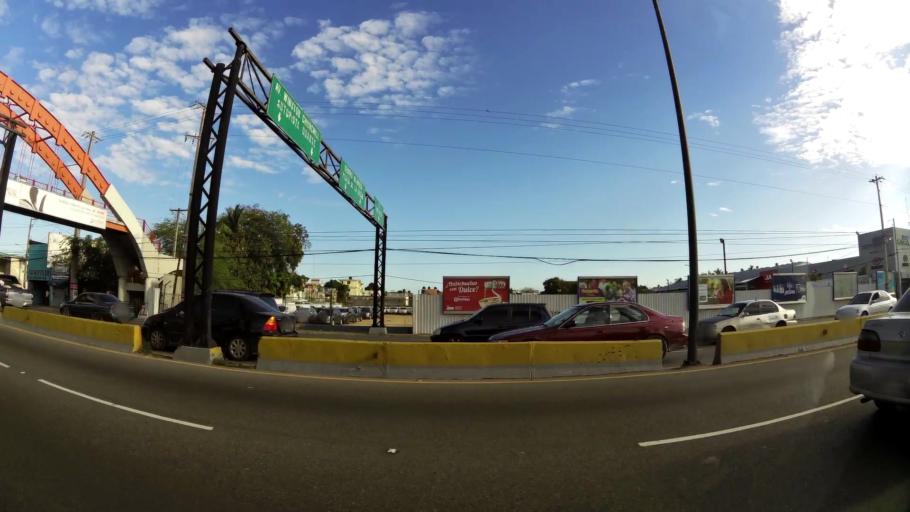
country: DO
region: Nacional
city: San Carlos
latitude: 18.4819
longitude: -69.9170
